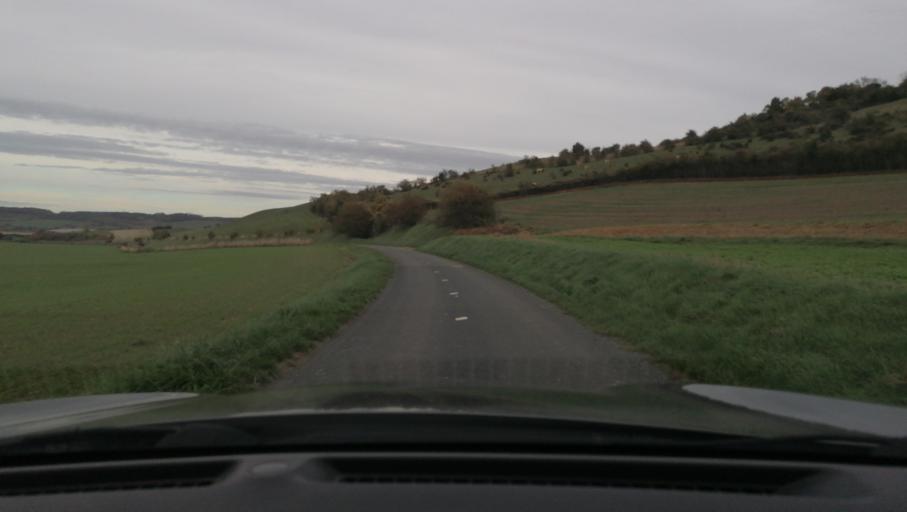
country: FR
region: Picardie
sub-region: Departement de la Somme
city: Bouttencourt
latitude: 49.8909
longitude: 1.6736
